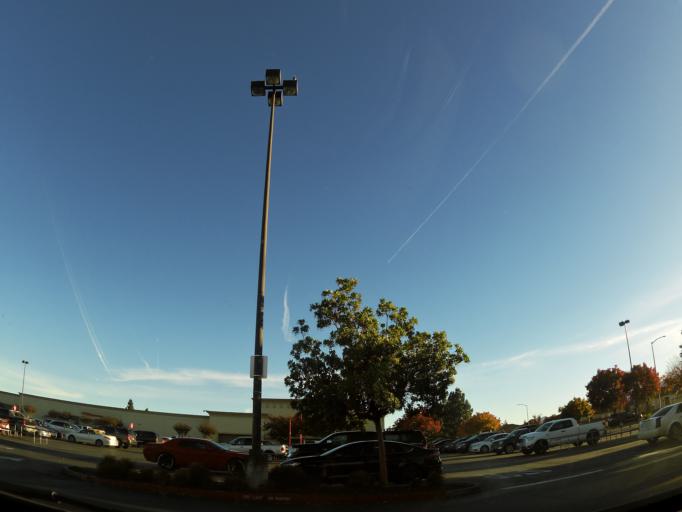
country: US
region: California
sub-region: San Benito County
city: Hollister
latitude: 36.8361
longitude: -121.3906
